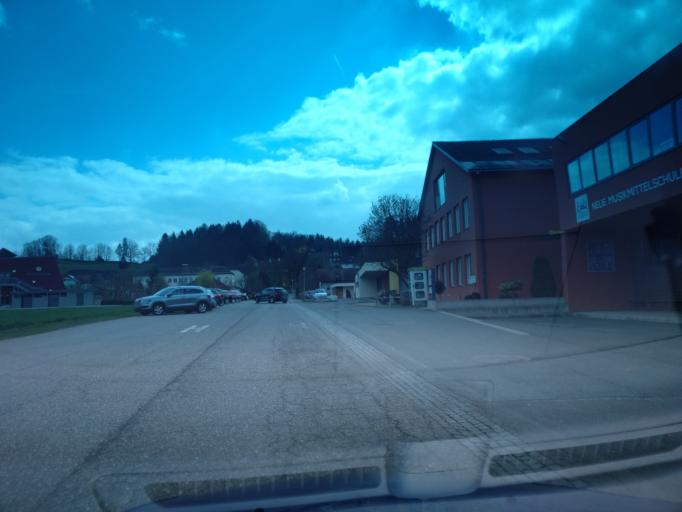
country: AT
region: Styria
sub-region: Politischer Bezirk Leibnitz
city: Grossklein
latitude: 46.7371
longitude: 15.4379
